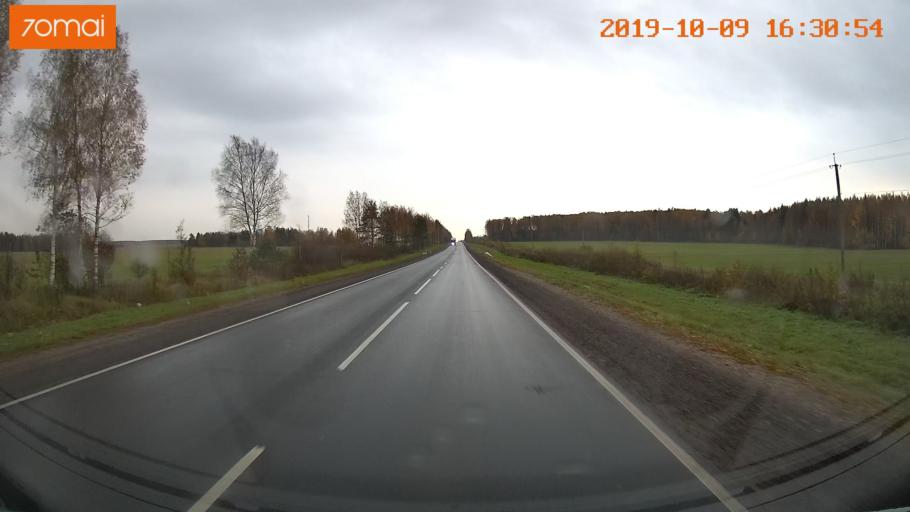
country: RU
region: Kostroma
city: Oktyabr'skiy
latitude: 57.6132
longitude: 40.9455
